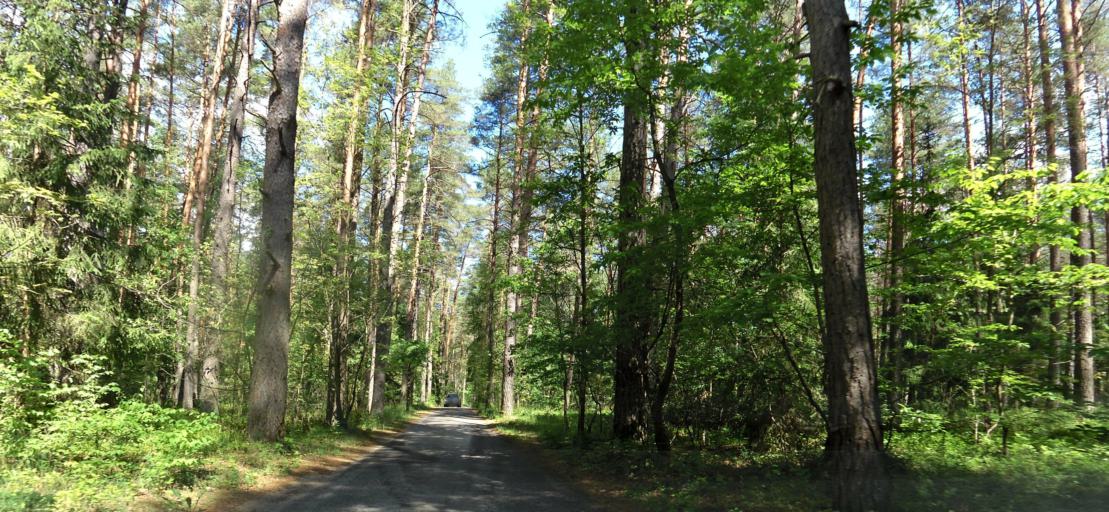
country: LT
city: Nemencine
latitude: 54.8095
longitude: 25.3942
